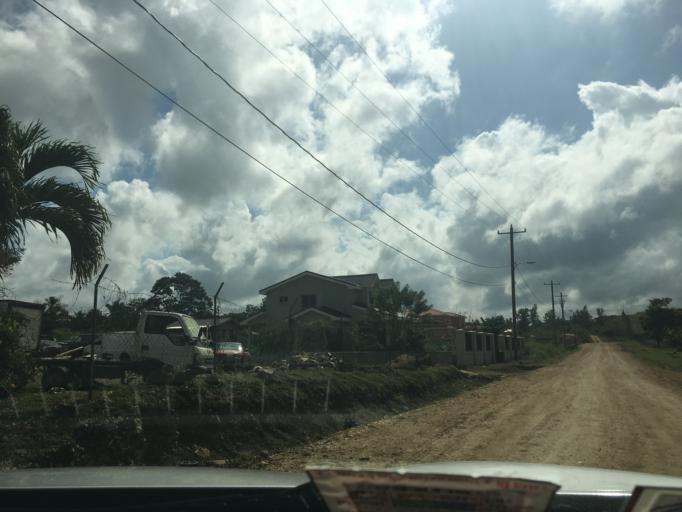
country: BZ
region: Cayo
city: Belmopan
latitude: 17.2508
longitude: -88.7887
